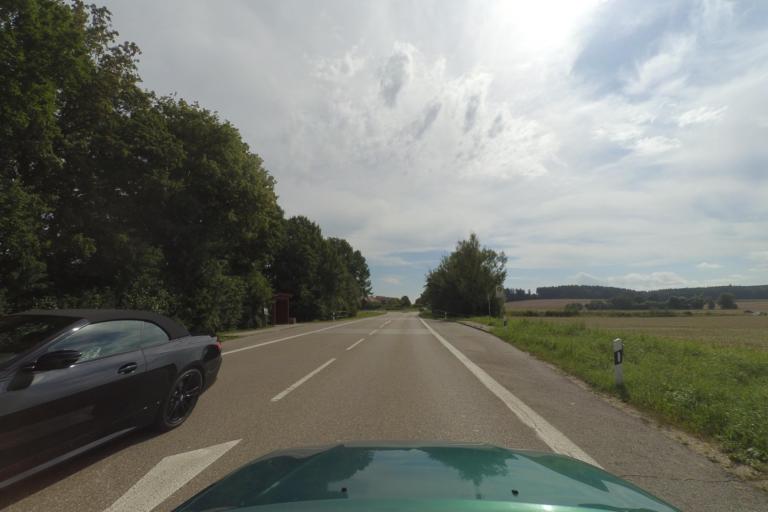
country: DE
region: Bavaria
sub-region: Lower Bavaria
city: Bad Abbach
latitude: 48.9361
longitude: 12.0610
